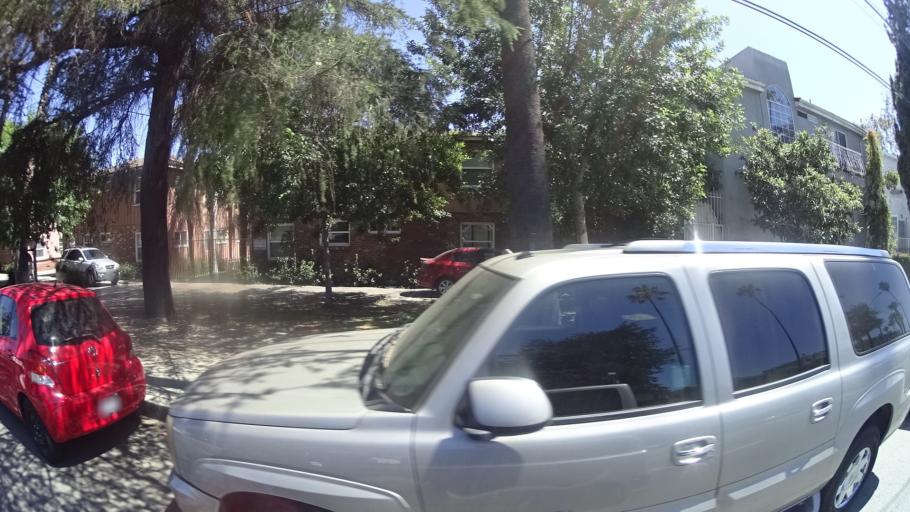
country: US
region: California
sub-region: Los Angeles County
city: Van Nuys
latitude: 34.2011
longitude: -118.4799
